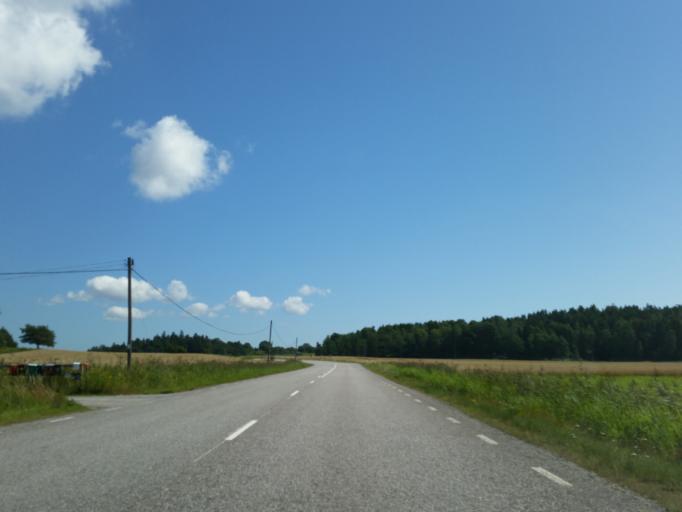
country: SE
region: Soedermanland
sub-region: Trosa Kommun
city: Vagnharad
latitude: 58.9874
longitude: 17.6285
